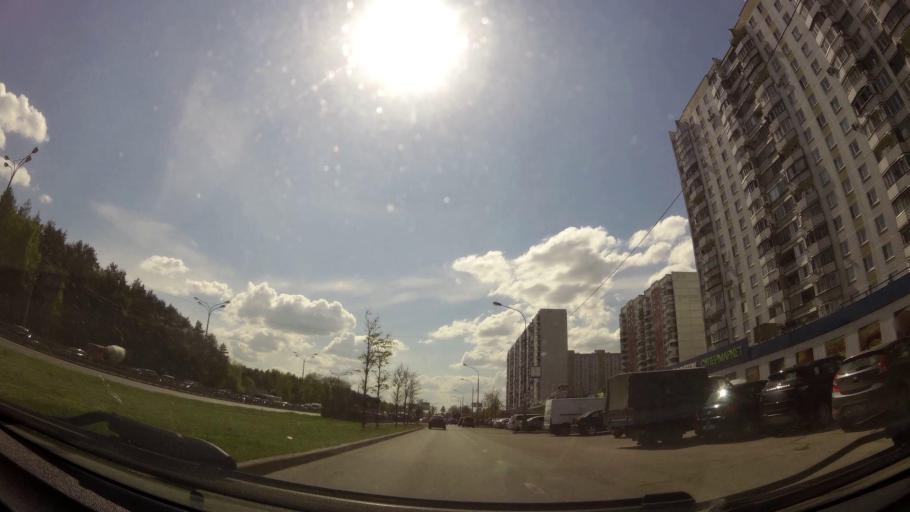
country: RU
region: Moscow
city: Novo-Peredelkino
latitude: 55.6362
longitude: 37.3492
